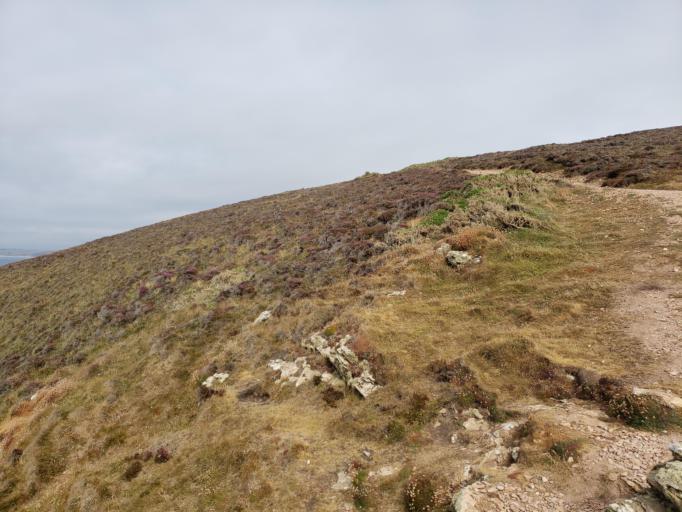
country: GB
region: England
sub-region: Cornwall
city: Saint Agnes
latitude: 50.3181
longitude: -5.2335
